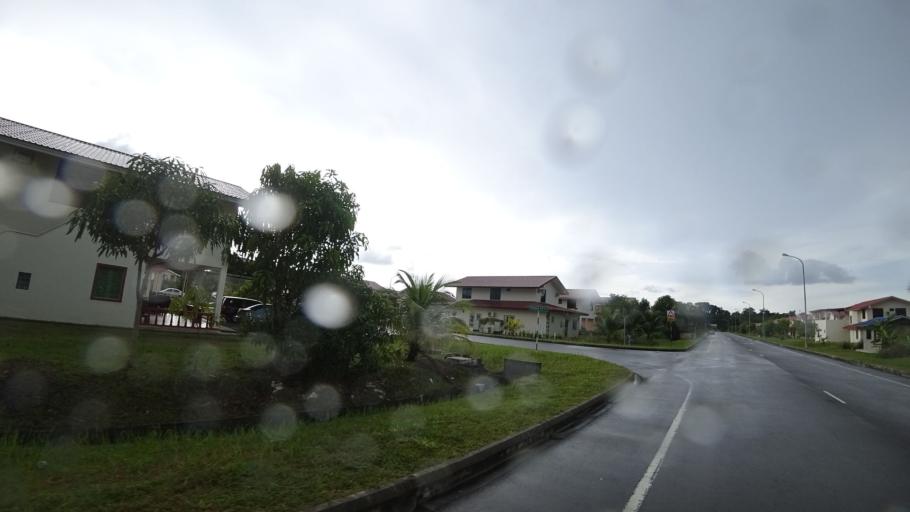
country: BN
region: Brunei and Muara
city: Bandar Seri Begawan
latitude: 4.8380
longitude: 114.9126
